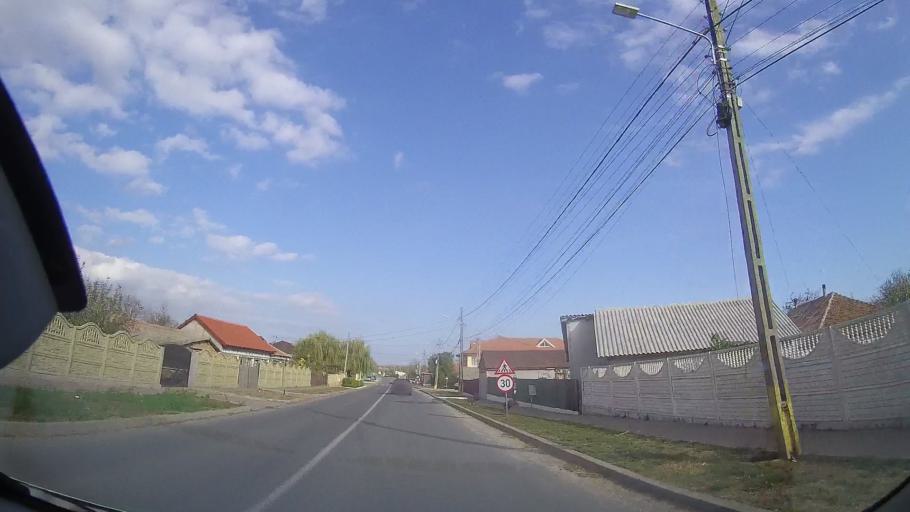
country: RO
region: Constanta
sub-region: Comuna Douazeci si Trei August
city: Dulcesti
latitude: 43.9047
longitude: 28.5445
